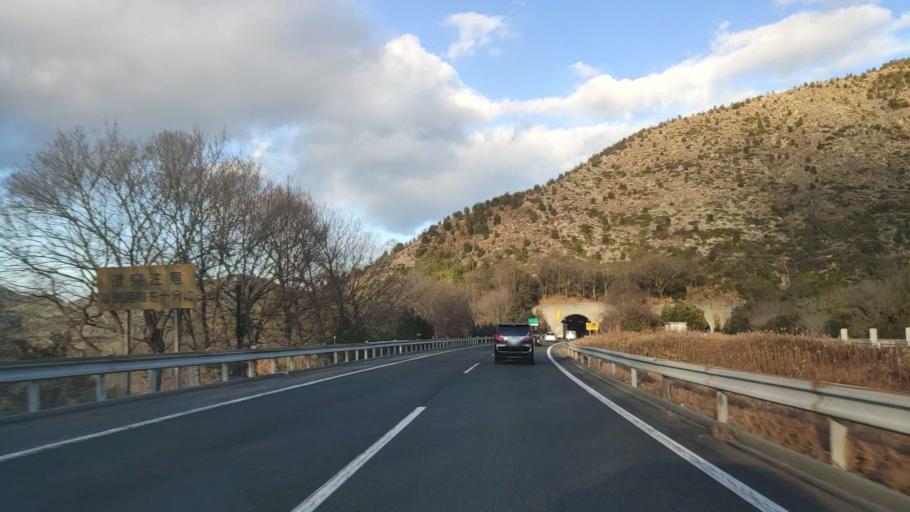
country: JP
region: Hyogo
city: Kariya
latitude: 34.7860
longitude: 134.3988
